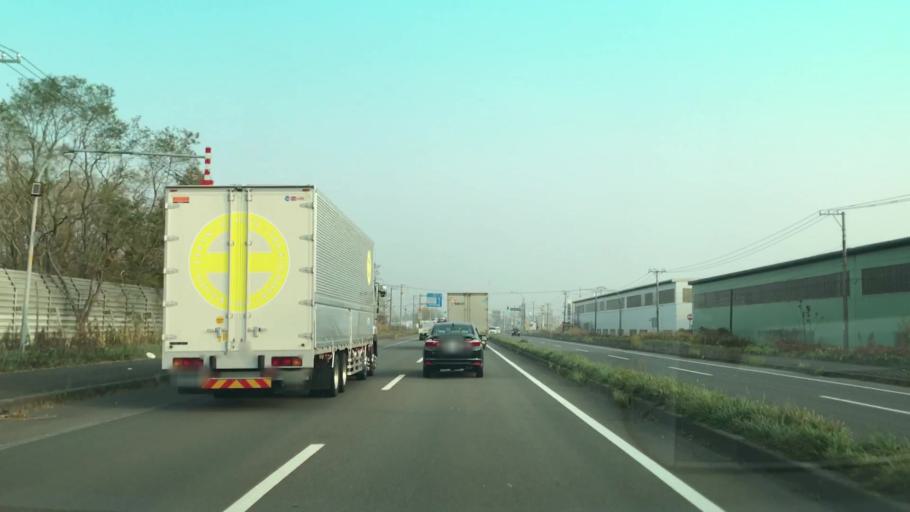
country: JP
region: Hokkaido
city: Ishikari
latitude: 43.1917
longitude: 141.3265
